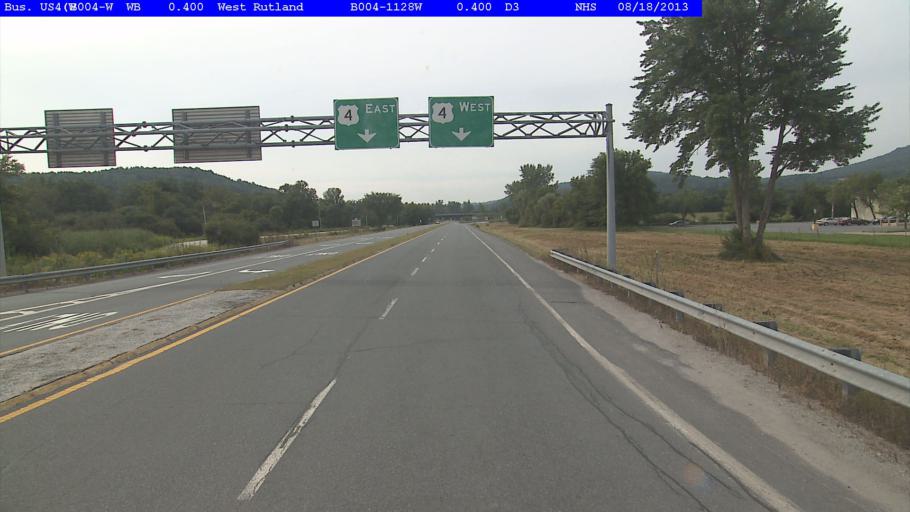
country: US
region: Vermont
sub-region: Rutland County
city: West Rutland
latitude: 43.5934
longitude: -73.0414
